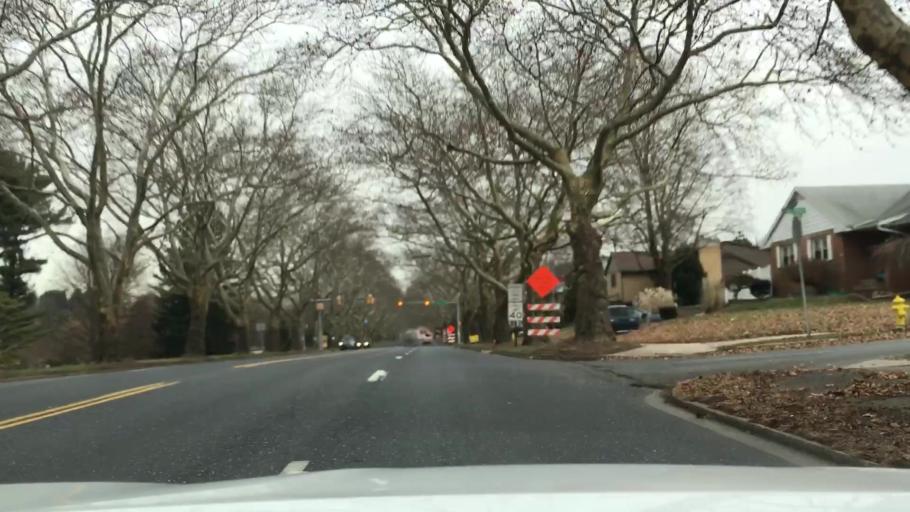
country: US
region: Pennsylvania
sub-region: Lehigh County
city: Dorneyville
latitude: 40.5922
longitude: -75.5081
